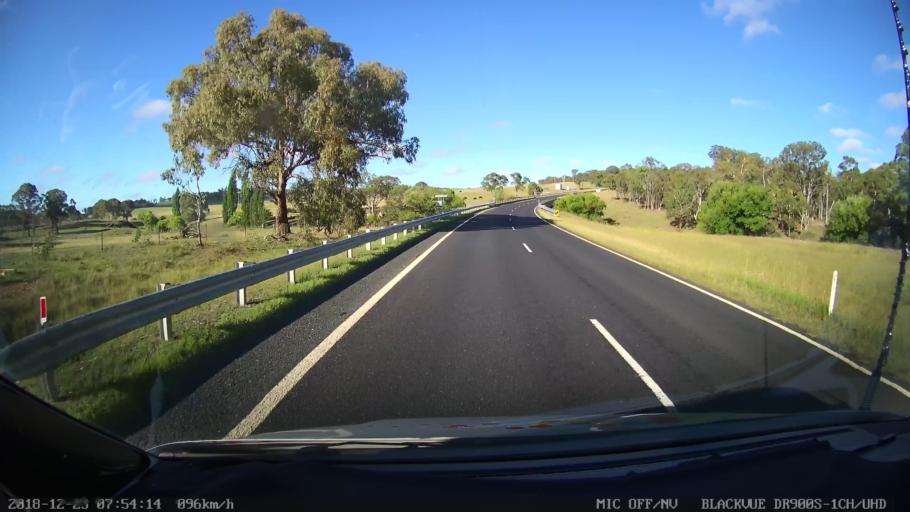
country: AU
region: New South Wales
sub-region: Armidale Dumaresq
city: Armidale
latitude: -30.5442
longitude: 151.7996
